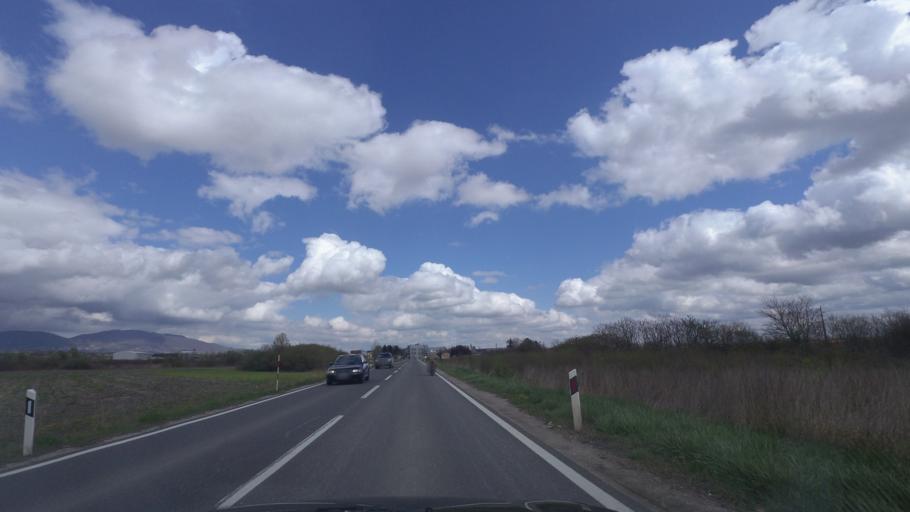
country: HR
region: Zagrebacka
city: Jastrebarsko
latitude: 45.6552
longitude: 15.6352
